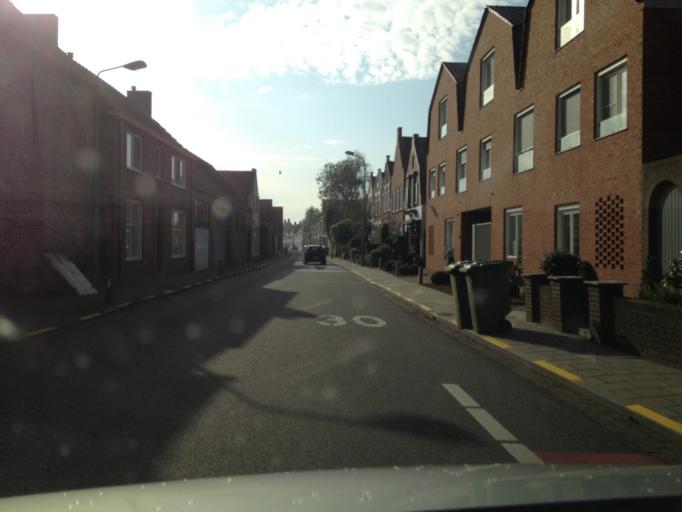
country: NL
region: Zeeland
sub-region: Gemeente Sluis
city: Sluis
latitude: 51.3124
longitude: 3.3878
